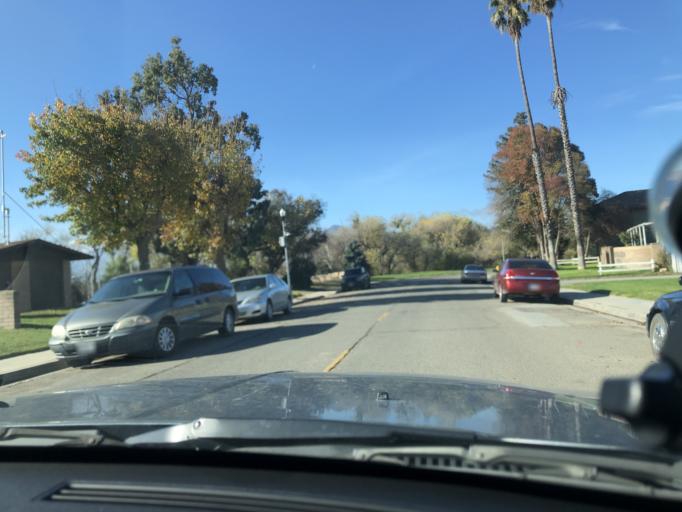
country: US
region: California
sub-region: Monterey County
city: King City
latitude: 36.2018
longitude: -121.1332
